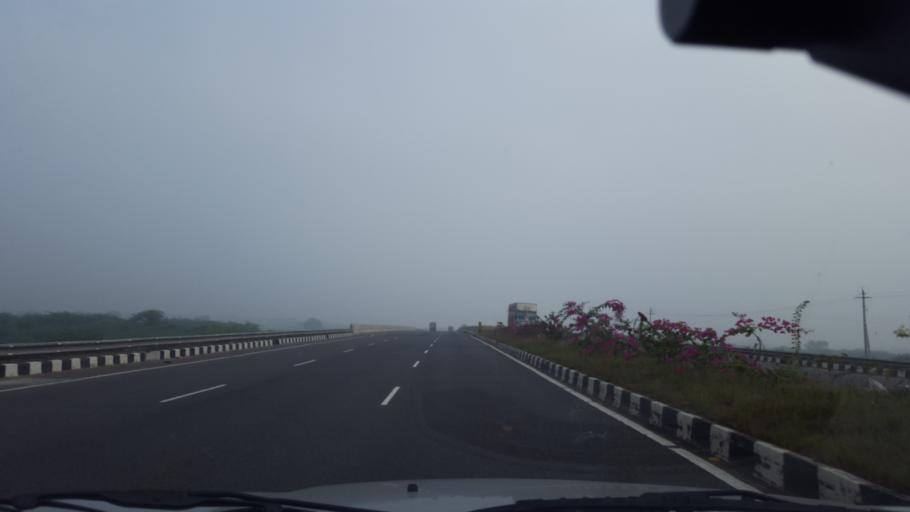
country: IN
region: Andhra Pradesh
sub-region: Prakasam
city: Ongole
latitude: 15.5029
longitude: 80.0708
